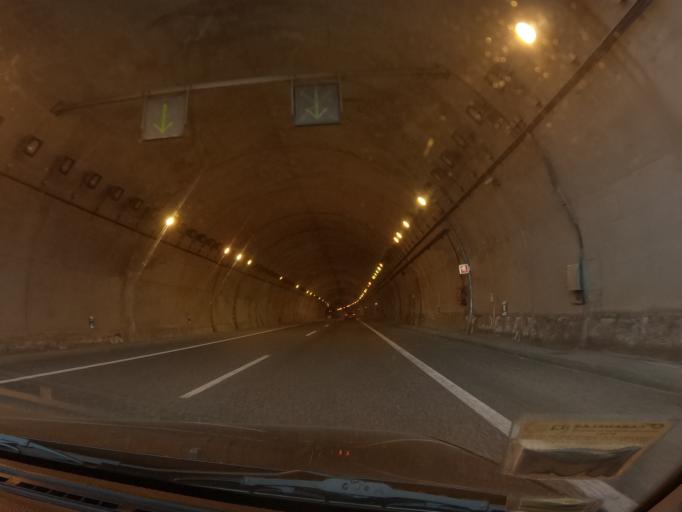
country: ES
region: Galicia
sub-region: Provincia de Lugo
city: Becerrea
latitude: 42.8740
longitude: -7.1761
